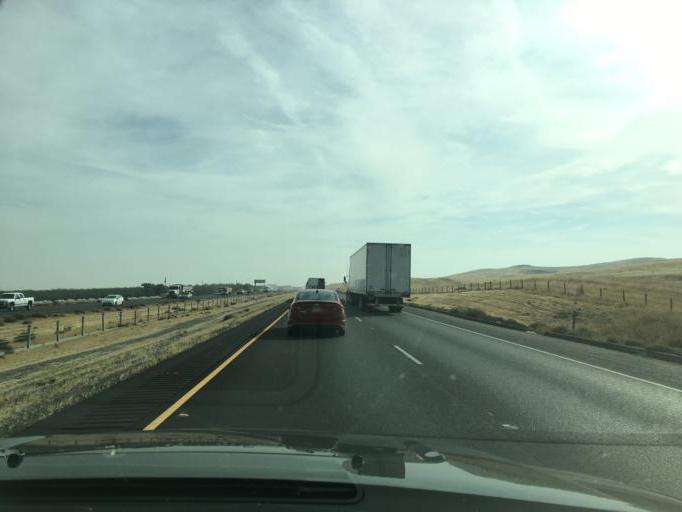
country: US
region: California
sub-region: Kings County
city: Avenal
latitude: 36.0630
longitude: -120.0793
